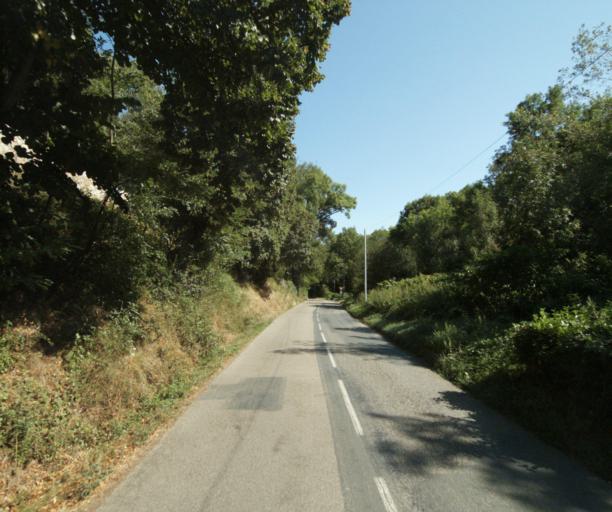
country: FR
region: Rhone-Alpes
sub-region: Departement du Rhone
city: Courzieu
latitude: 45.7501
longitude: 4.5622
